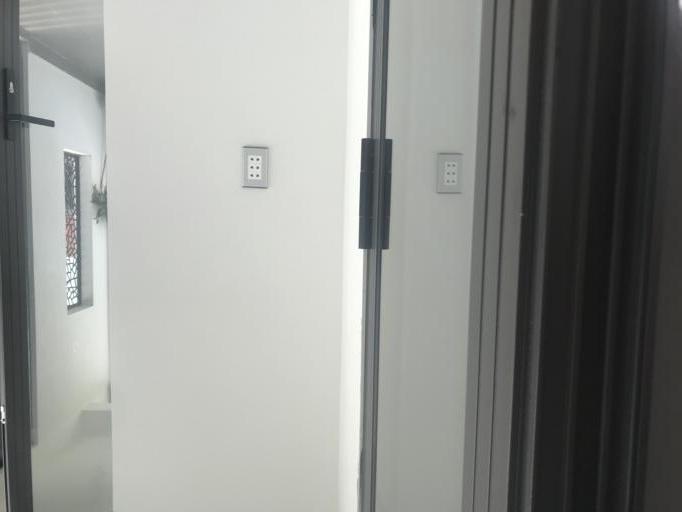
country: VN
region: Quang Tri
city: Dong Ha
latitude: 16.8084
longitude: 107.1054
